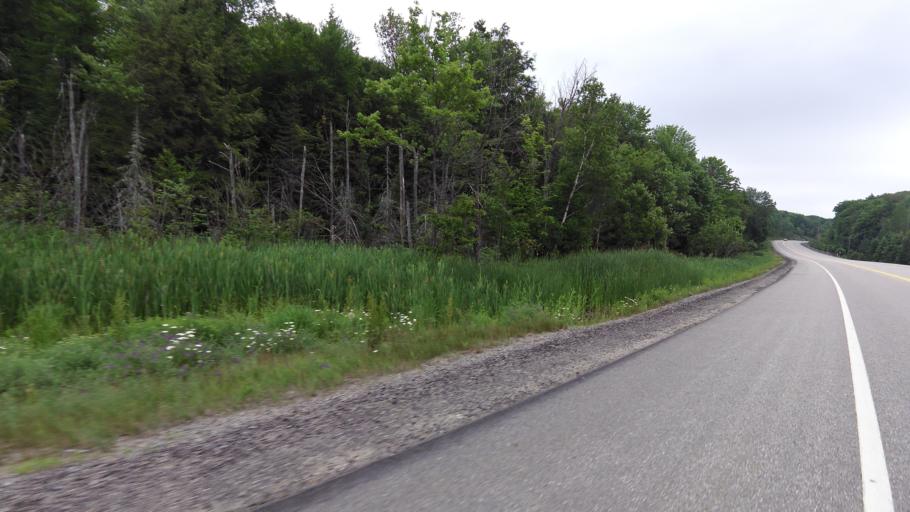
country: CA
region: Ontario
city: Huntsville
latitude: 45.3327
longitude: -78.9560
